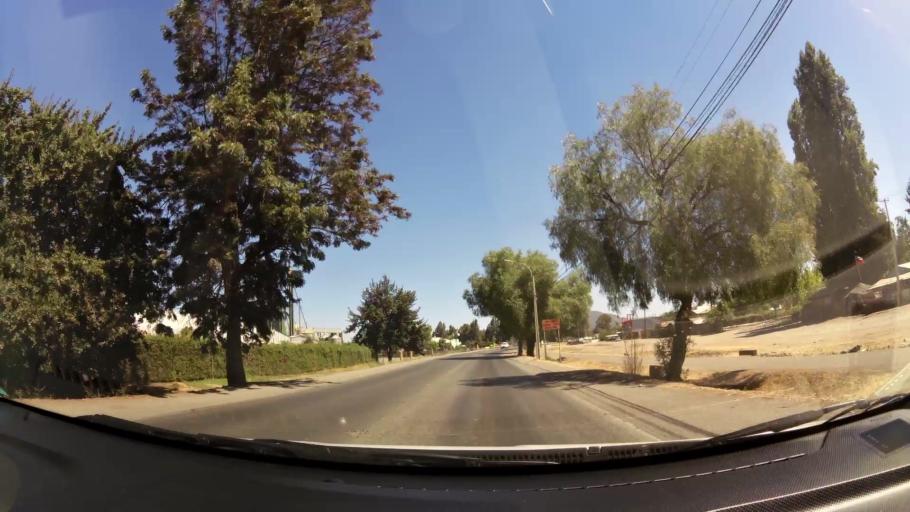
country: CL
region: O'Higgins
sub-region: Provincia de Colchagua
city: Chimbarongo
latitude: -34.5771
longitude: -70.9754
